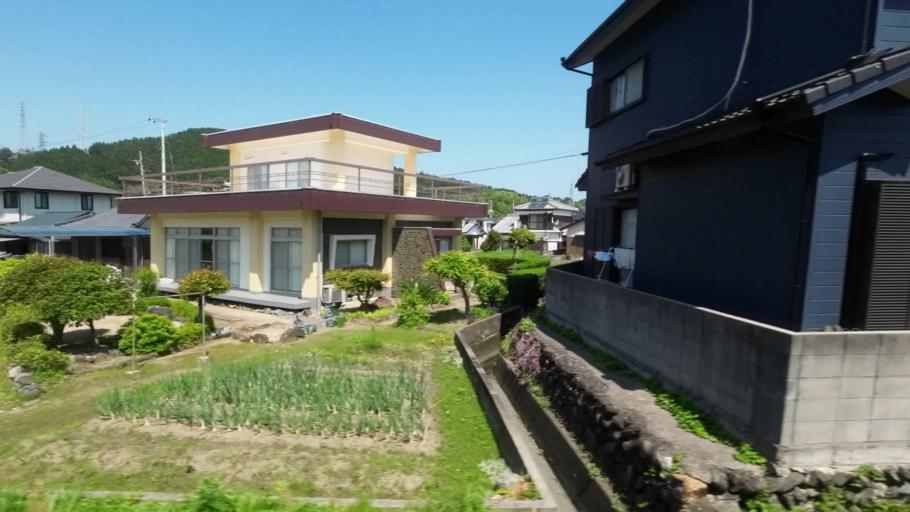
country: JP
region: Ehime
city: Niihama
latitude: 33.9379
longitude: 133.2833
